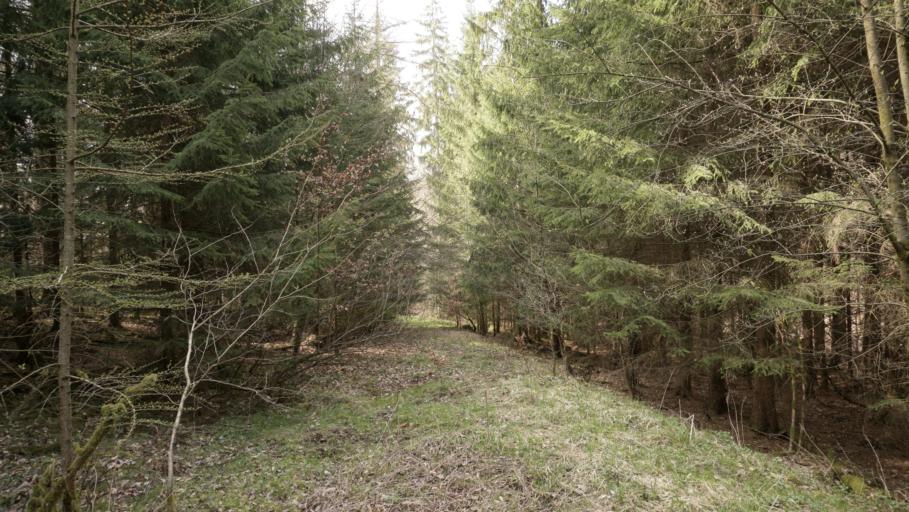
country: DE
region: Baden-Wuerttemberg
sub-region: Karlsruhe Region
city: Neckargerach
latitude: 49.4117
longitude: 9.1061
